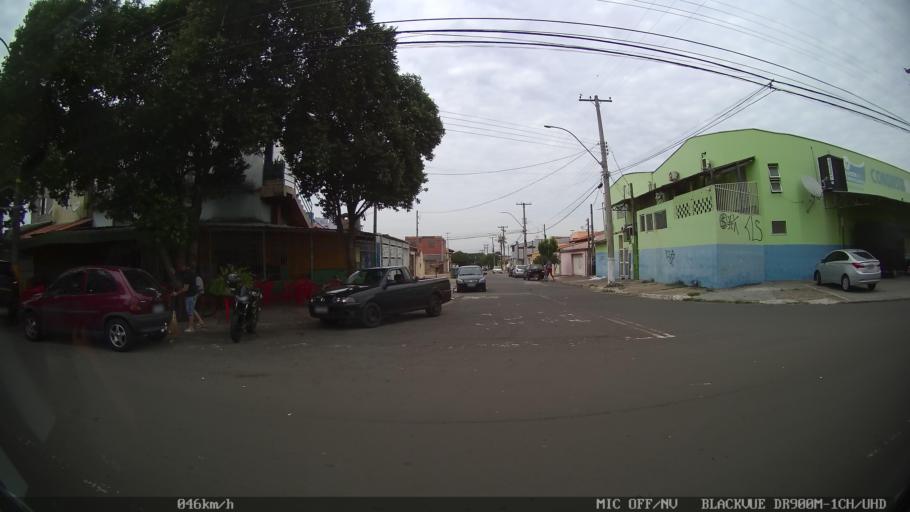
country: BR
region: Sao Paulo
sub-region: Paulinia
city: Paulinia
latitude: -22.7192
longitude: -47.1736
